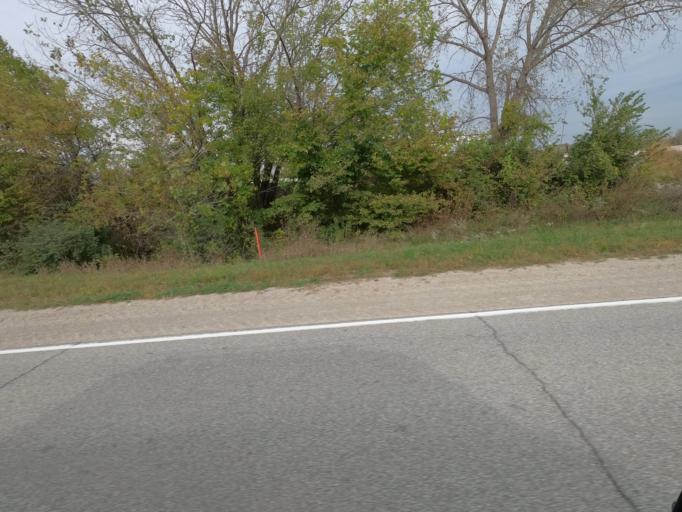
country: US
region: Iowa
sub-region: Van Buren County
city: Keosauqua
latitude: 40.8653
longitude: -92.1412
